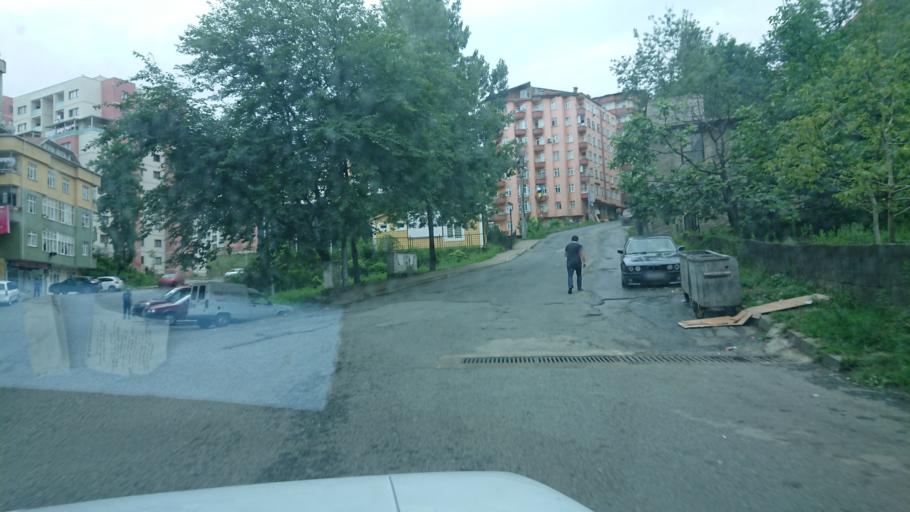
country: TR
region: Rize
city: Rize
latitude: 41.0183
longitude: 40.5160
